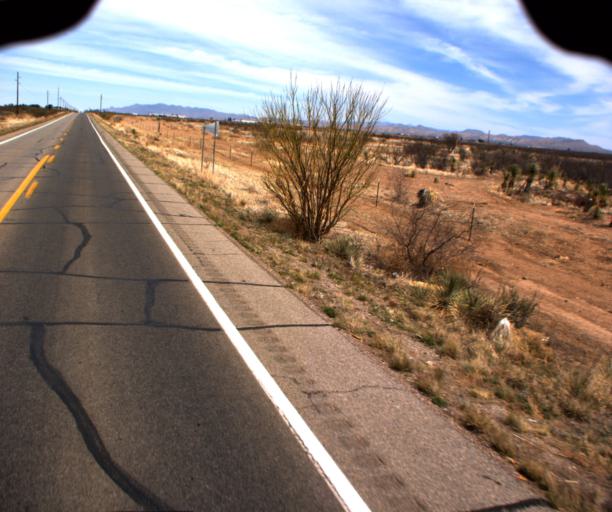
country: US
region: Arizona
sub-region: Cochise County
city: Pirtleville
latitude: 31.3750
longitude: -109.5793
